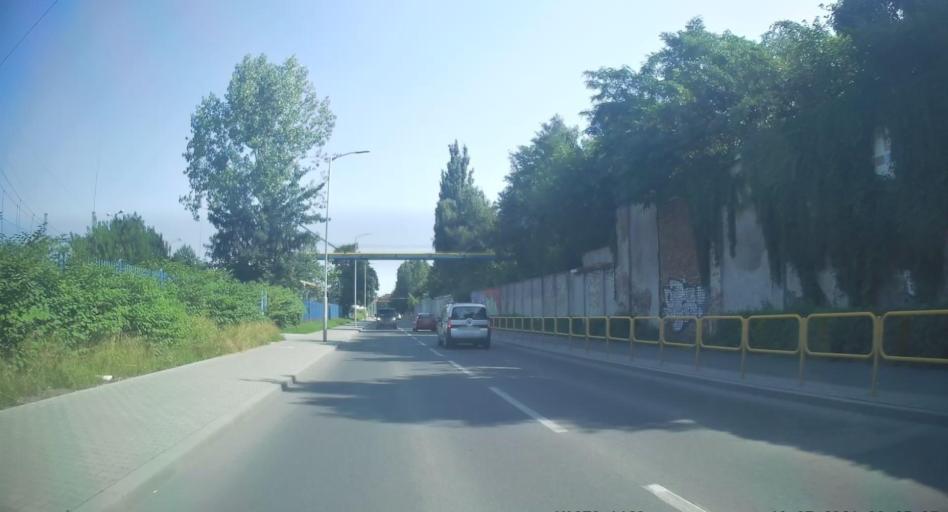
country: PL
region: Silesian Voivodeship
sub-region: Swietochlowice
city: Swietochlowice
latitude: 50.2844
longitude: 18.9133
